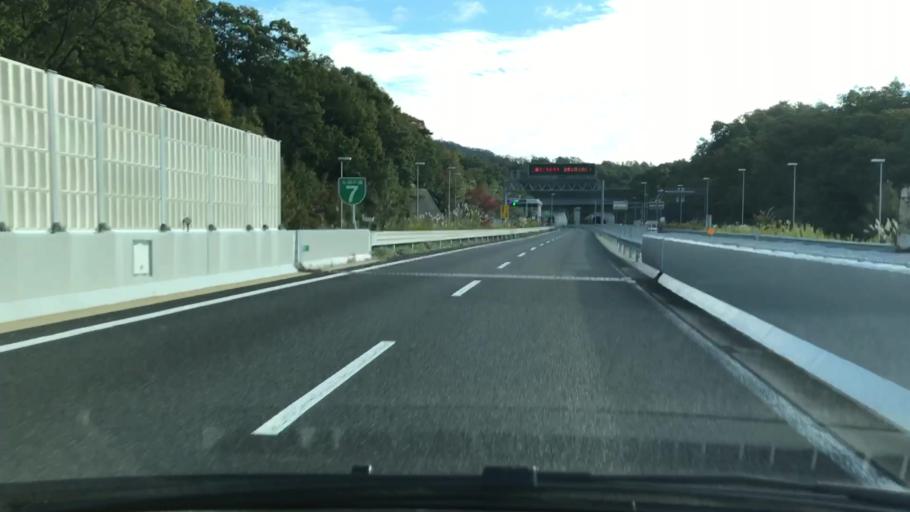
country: JP
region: Hyogo
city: Sandacho
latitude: 34.8185
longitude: 135.2513
